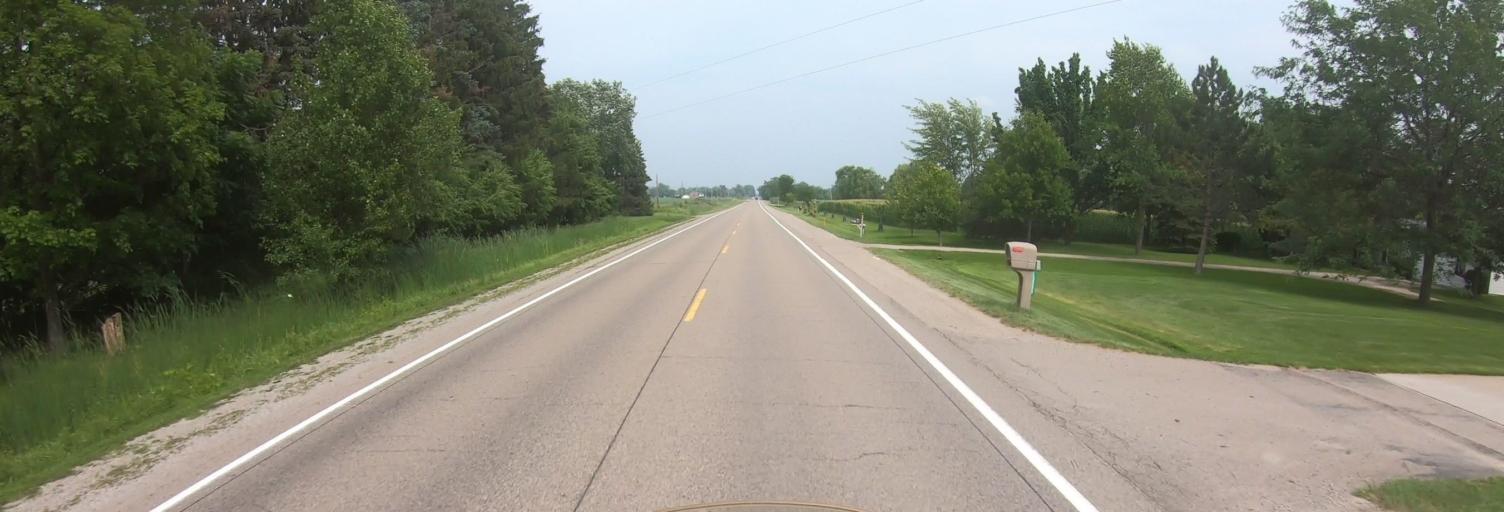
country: US
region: Michigan
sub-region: Genesee County
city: Swartz Creek
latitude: 42.9569
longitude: -83.8851
